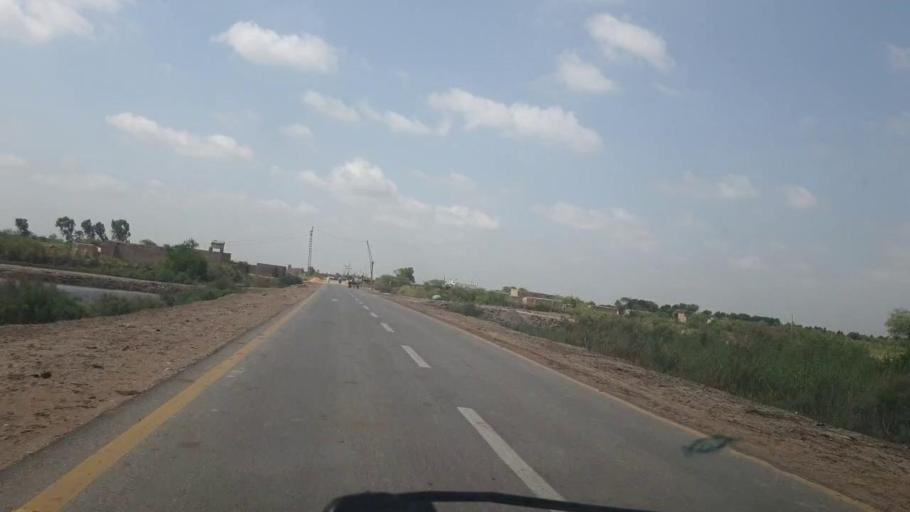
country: PK
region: Sindh
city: Berani
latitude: 25.6861
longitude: 68.9271
